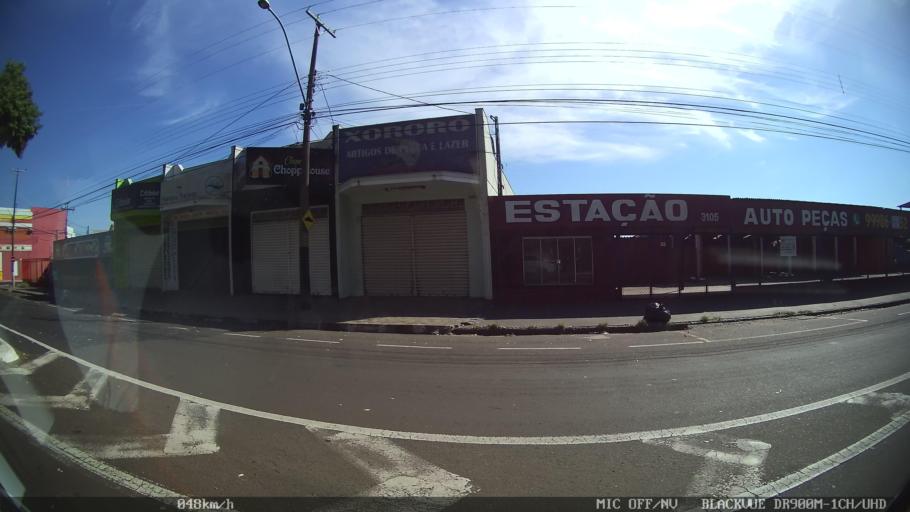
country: BR
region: Sao Paulo
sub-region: Franca
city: Franca
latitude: -20.5235
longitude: -47.4108
